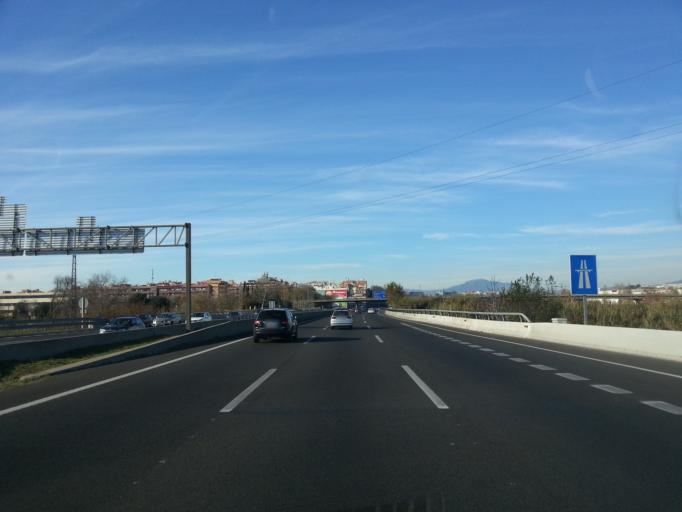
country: ES
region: Catalonia
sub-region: Provincia de Barcelona
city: Ripollet
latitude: 41.4904
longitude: 2.1554
